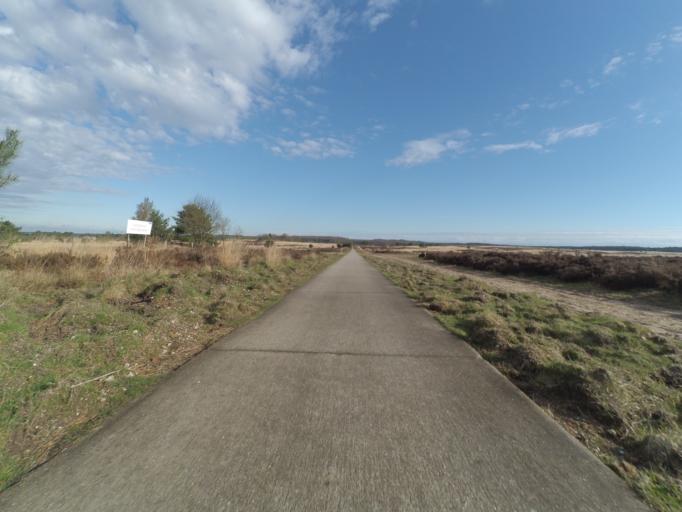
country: NL
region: Gelderland
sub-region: Gemeente Ede
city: Otterlo
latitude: 52.1595
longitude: 5.8475
